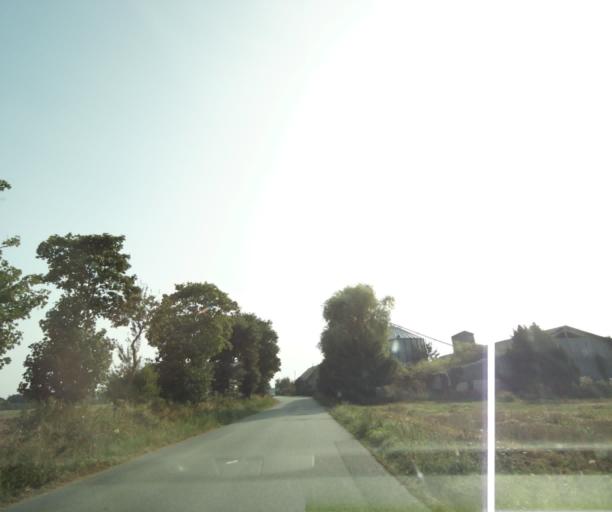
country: FR
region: Brittany
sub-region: Departement des Cotes-d'Armor
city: Jugon-les-Lacs
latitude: 48.4191
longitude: -2.3139
